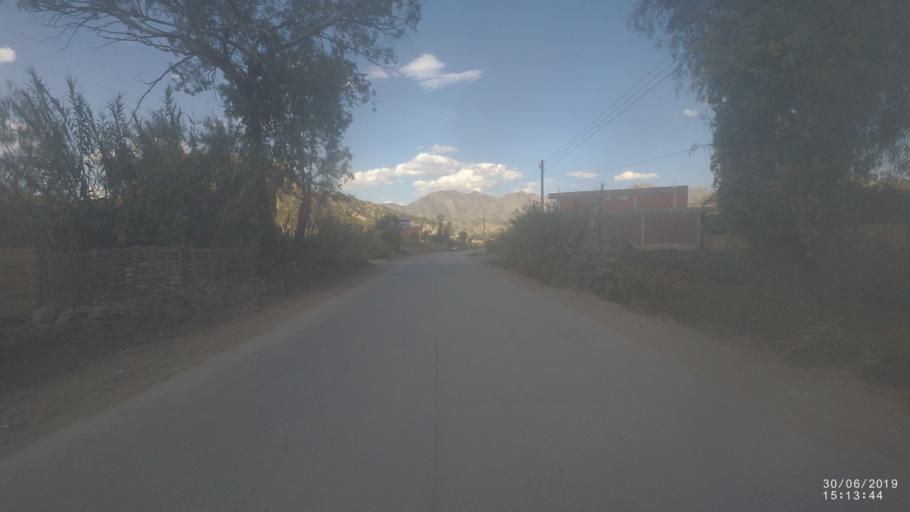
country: BO
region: Cochabamba
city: Irpa Irpa
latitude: -17.7230
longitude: -66.2807
